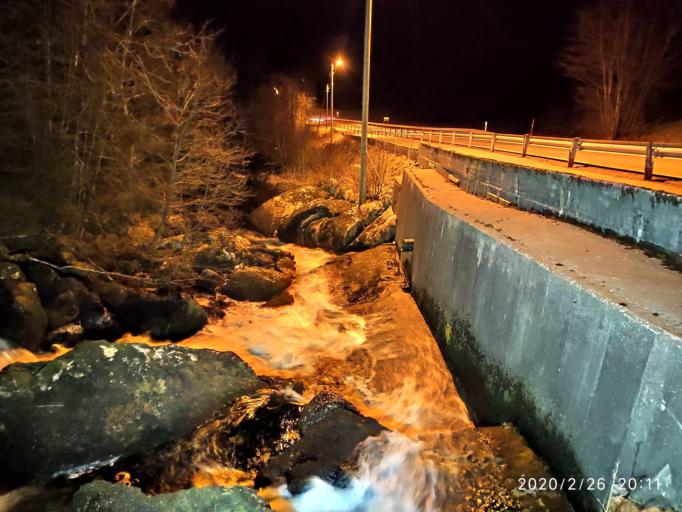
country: NO
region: Hordaland
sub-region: Tysnes
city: Uggdal
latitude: 60.0108
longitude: 5.5040
